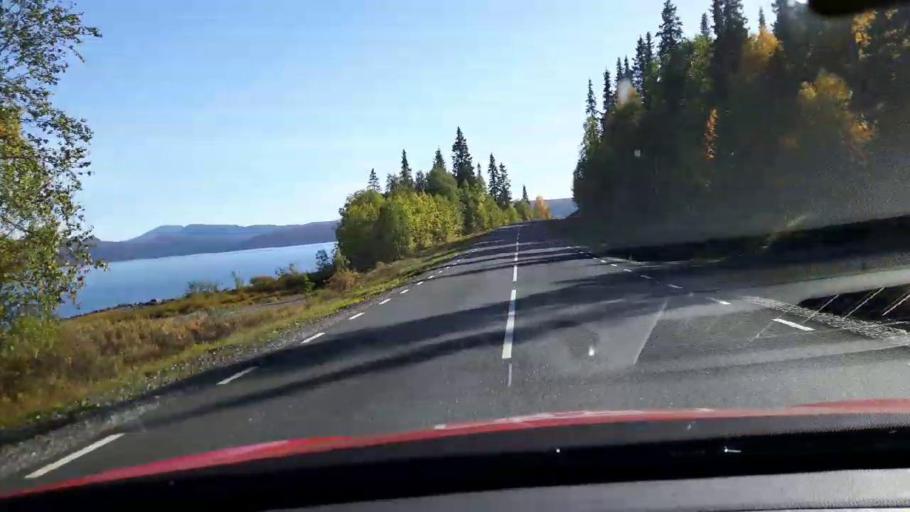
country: NO
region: Nord-Trondelag
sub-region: Royrvik
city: Royrvik
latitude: 64.8325
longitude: 14.0777
